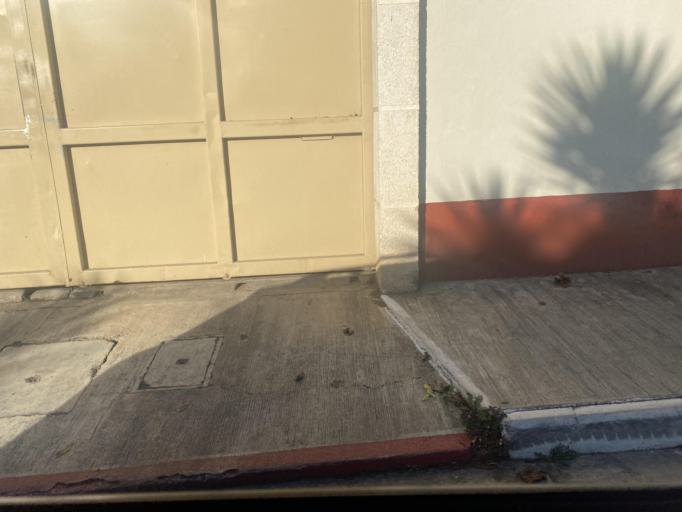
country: GT
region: Quetzaltenango
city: Quetzaltenango
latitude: 14.8544
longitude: -91.5207
